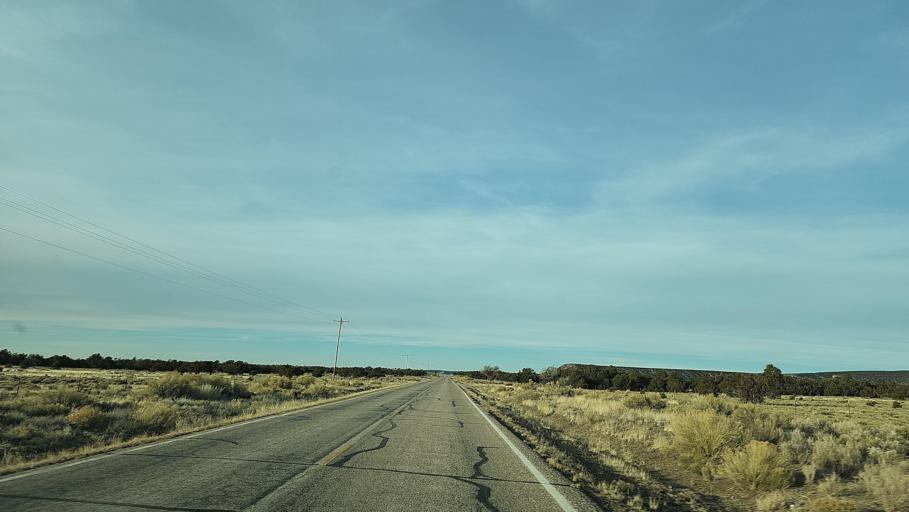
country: US
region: New Mexico
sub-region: McKinley County
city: Black Rock
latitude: 34.4418
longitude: -108.4271
